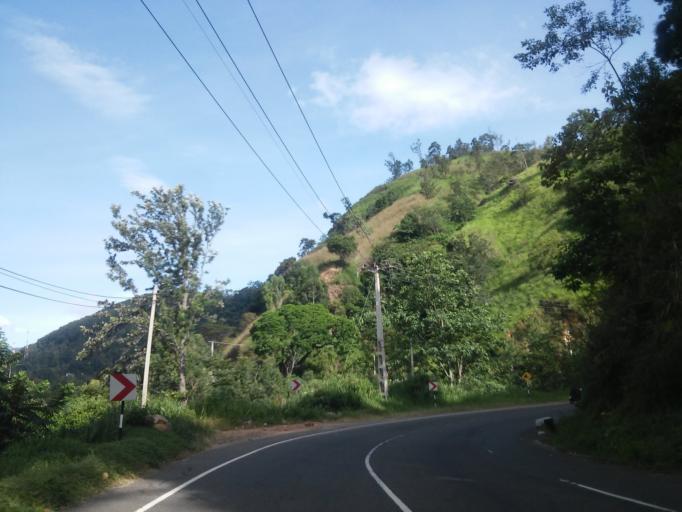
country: LK
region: Uva
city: Haputale
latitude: 6.7645
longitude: 80.8980
